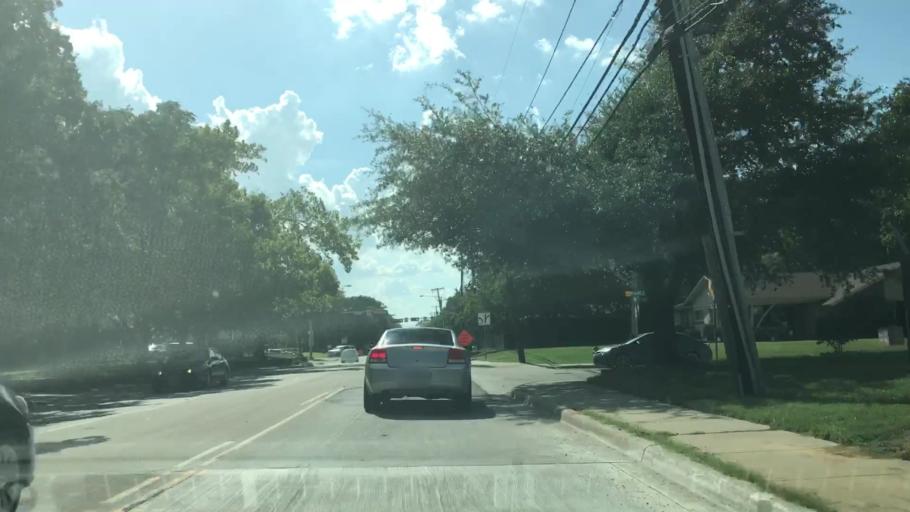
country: US
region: Texas
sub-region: Dallas County
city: Irving
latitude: 32.8295
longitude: -96.9498
